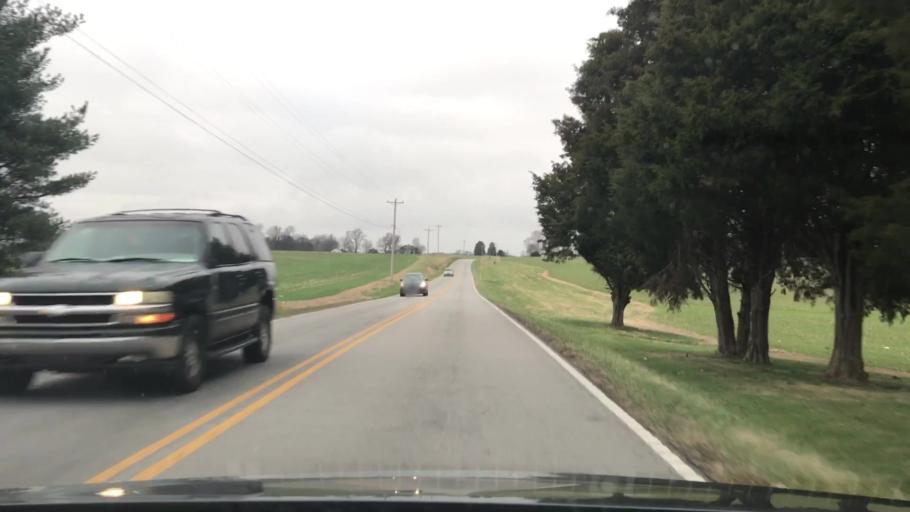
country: US
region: Kentucky
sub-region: Todd County
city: Guthrie
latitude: 36.6518
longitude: -87.1999
